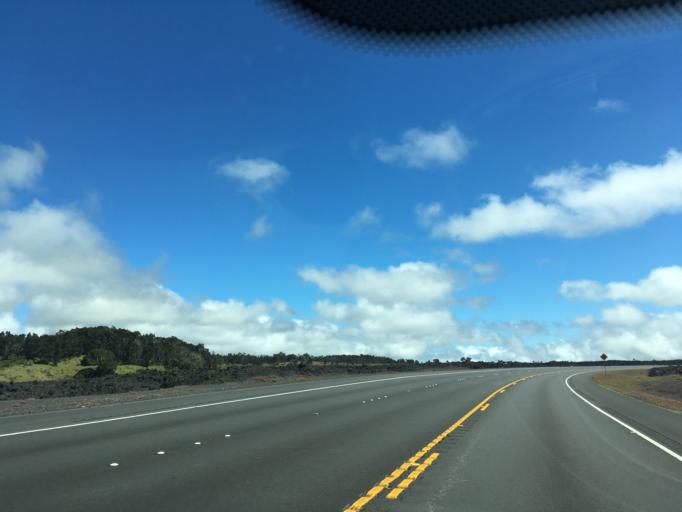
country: US
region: Hawaii
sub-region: Hawaii County
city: Volcano
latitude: 19.6815
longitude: -155.3946
